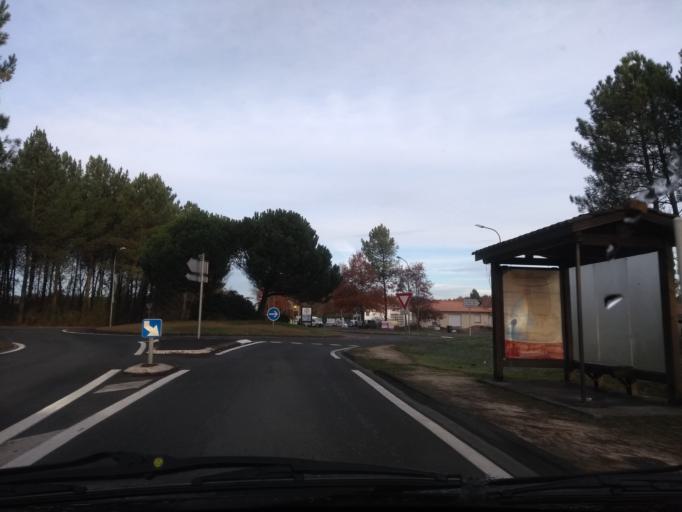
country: FR
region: Aquitaine
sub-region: Departement de la Gironde
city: Salles
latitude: 44.5599
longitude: -0.8745
